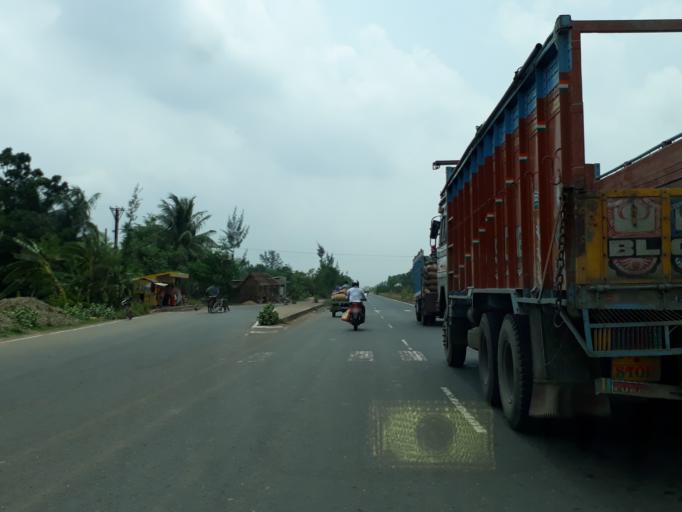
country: IN
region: West Bengal
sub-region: Purba Medinipur
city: Monoharpur
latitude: 22.1125
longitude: 88.0111
